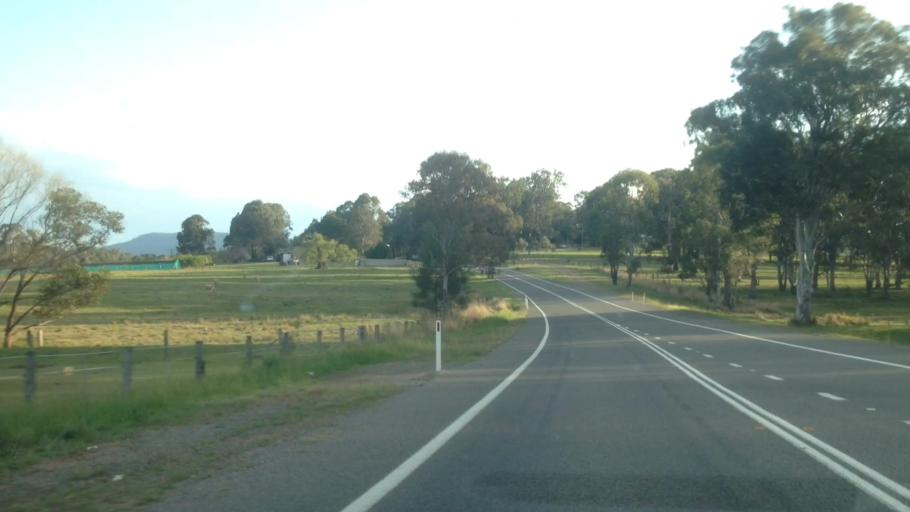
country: AU
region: New South Wales
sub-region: Cessnock
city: Kurri Kurri
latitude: -32.8636
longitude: 151.4812
